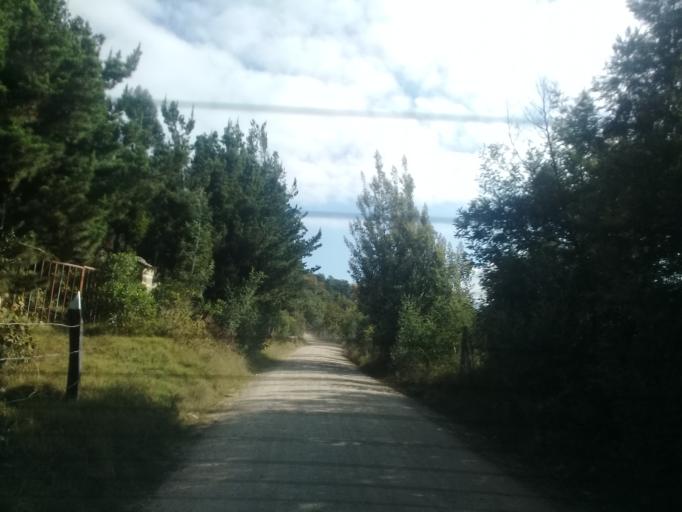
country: CO
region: Cundinamarca
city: Guatavita
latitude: 4.9411
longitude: -73.8704
